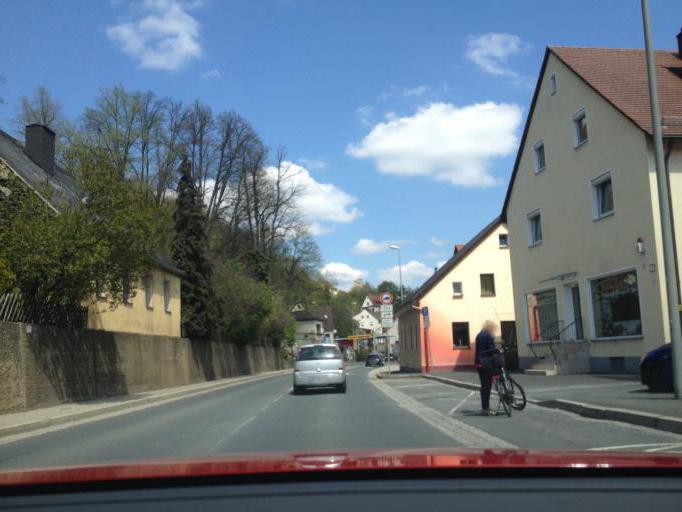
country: DE
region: Bavaria
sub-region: Upper Franconia
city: Pegnitz
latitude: 49.7558
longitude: 11.5364
